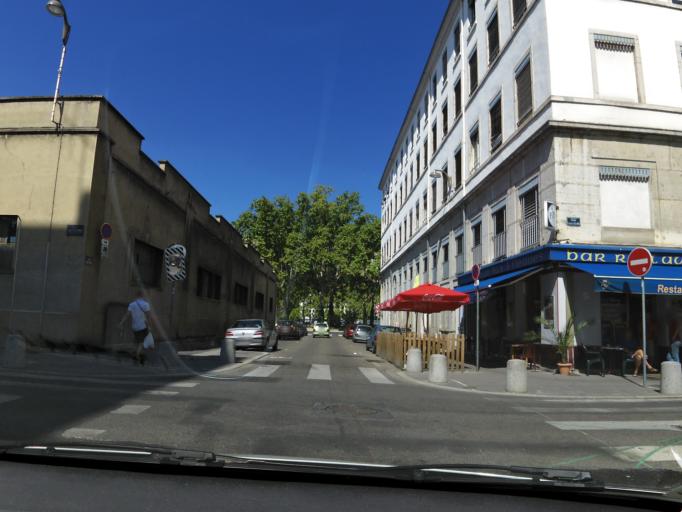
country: FR
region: Rhone-Alpes
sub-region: Departement du Rhone
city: Lyon
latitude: 45.7492
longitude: 4.8221
